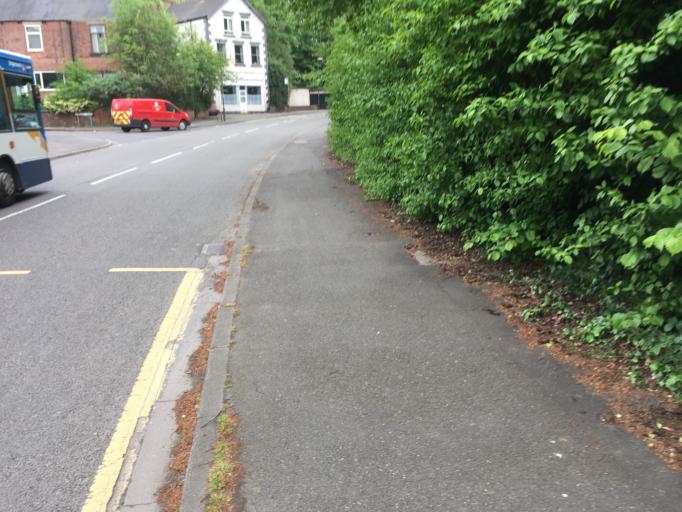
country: GB
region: England
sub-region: Derbyshire
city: Chesterfield
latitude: 53.2307
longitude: -1.4170
